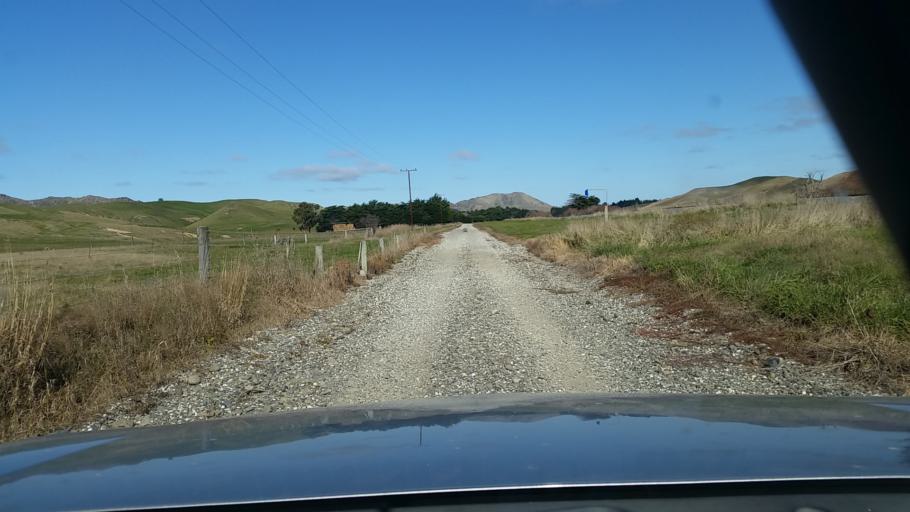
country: NZ
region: Marlborough
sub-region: Marlborough District
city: Blenheim
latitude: -41.7474
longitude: 174.1578
